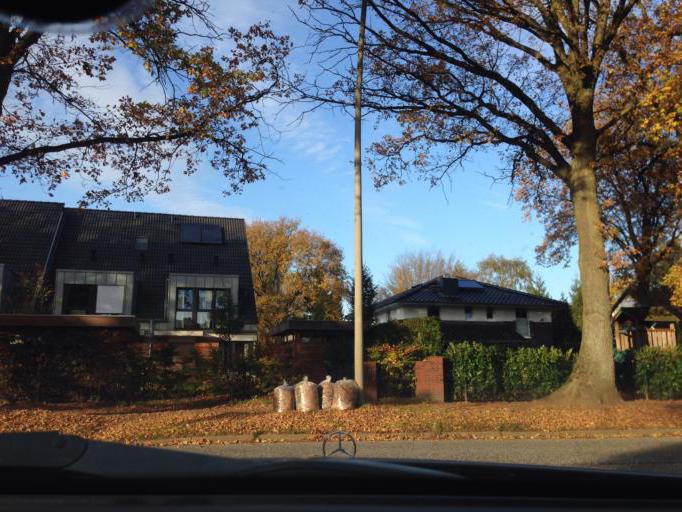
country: DE
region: Schleswig-Holstein
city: Barsbuettel
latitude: 53.5937
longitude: 10.1815
